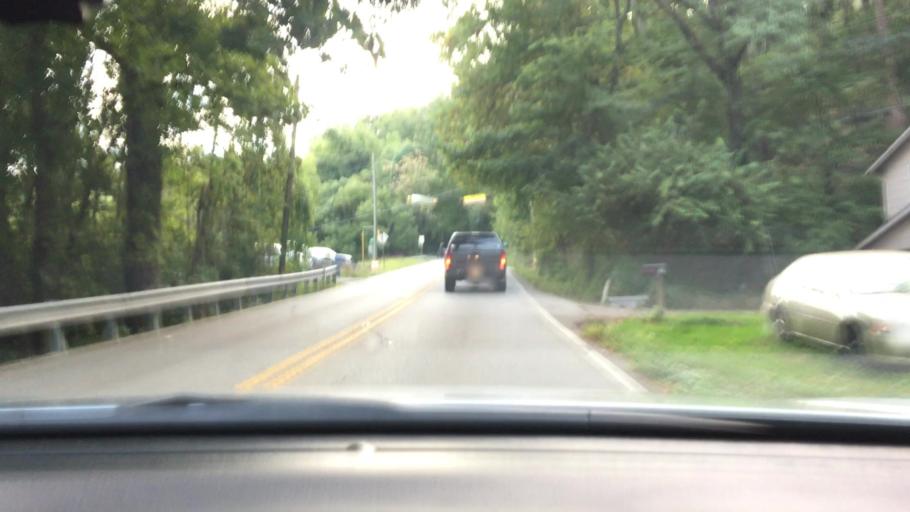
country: US
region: Tennessee
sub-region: Hamilton County
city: Lookout Mountain
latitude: 35.0047
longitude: -85.3315
